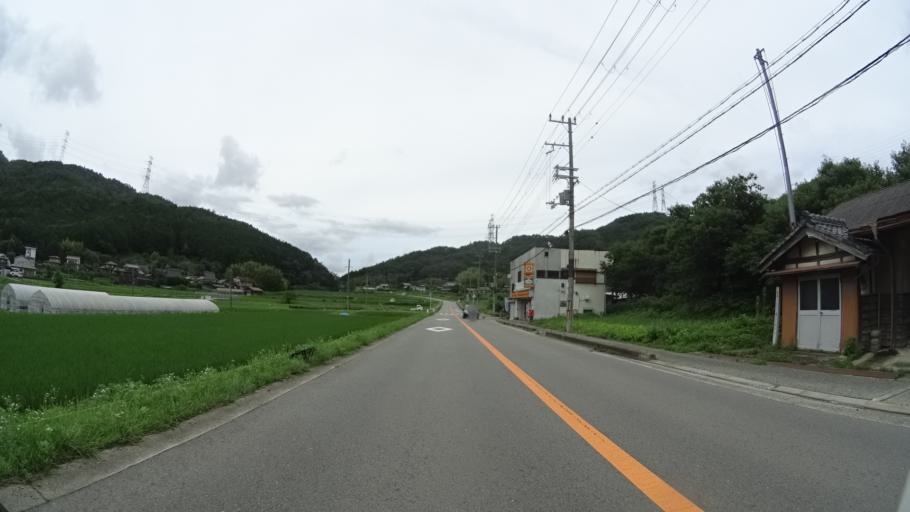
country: JP
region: Kyoto
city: Kameoka
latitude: 34.9873
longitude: 135.4751
